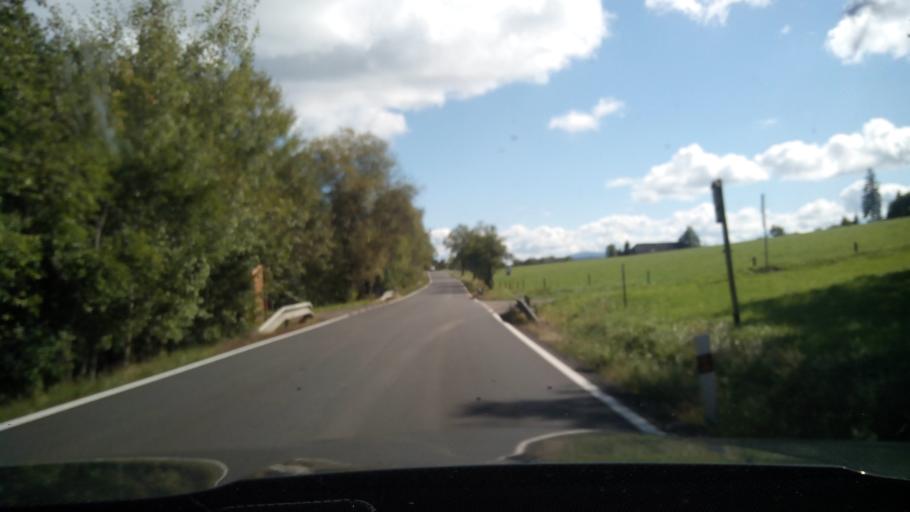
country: CZ
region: Jihocesky
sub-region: Okres Prachatice
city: Stachy
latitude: 49.1131
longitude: 13.6479
